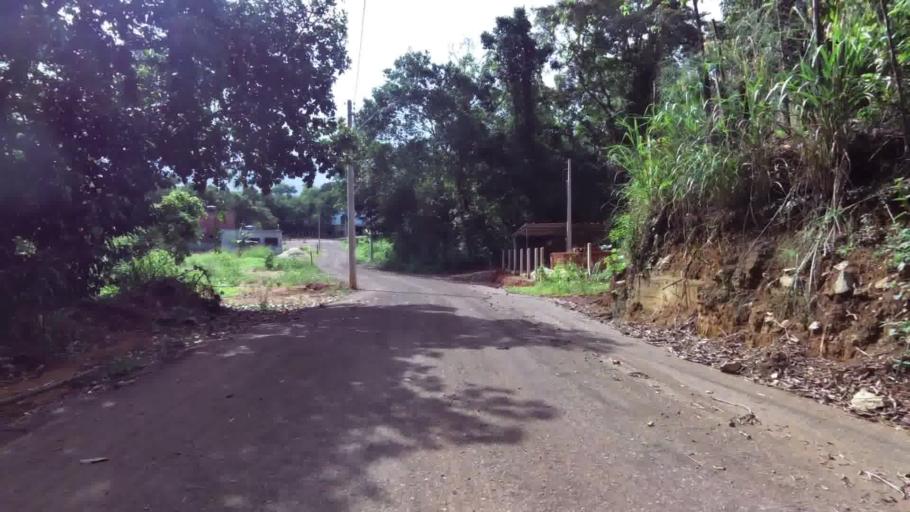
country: BR
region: Espirito Santo
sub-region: Piuma
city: Piuma
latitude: -20.8286
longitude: -40.6982
